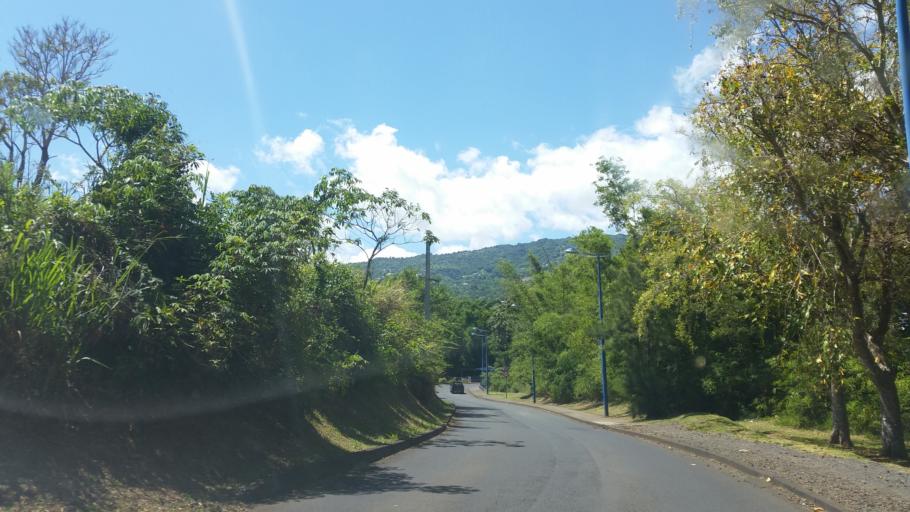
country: RE
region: Reunion
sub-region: Reunion
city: Sainte-Marie
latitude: -20.9254
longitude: 55.5274
